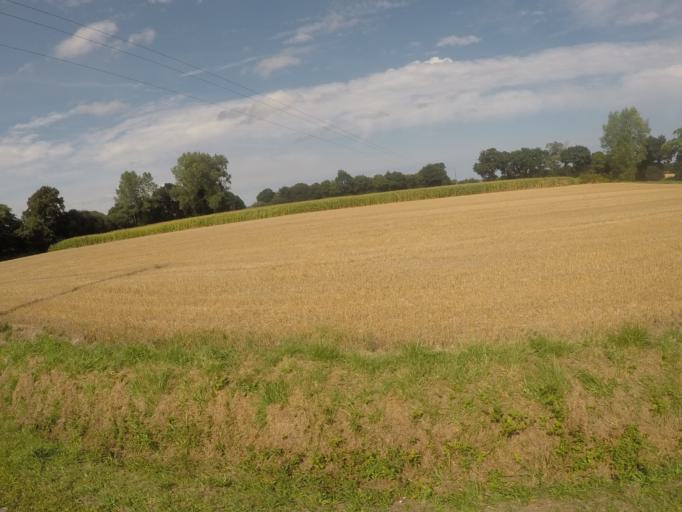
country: FR
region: Brittany
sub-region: Departement des Cotes-d'Armor
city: Goudelin
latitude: 48.6033
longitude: -3.0091
